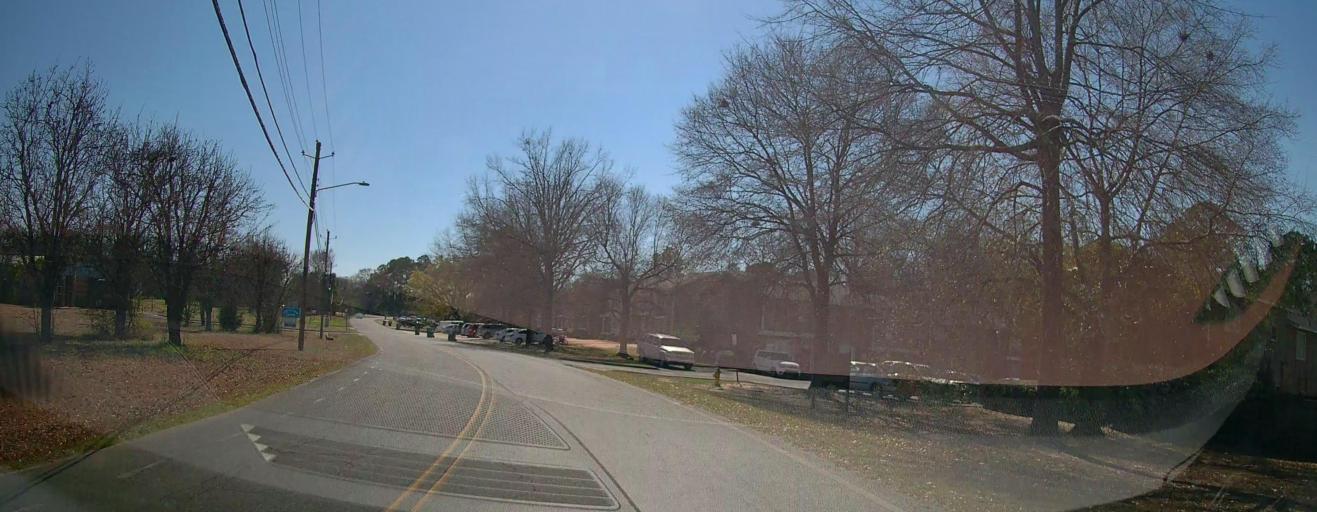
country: US
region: Georgia
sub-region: Houston County
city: Perry
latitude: 32.4582
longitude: -83.7127
